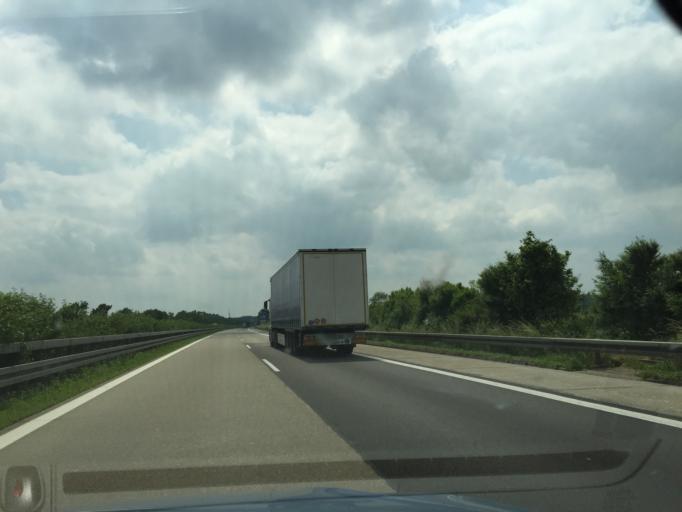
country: DE
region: Baden-Wuerttemberg
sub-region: Regierungsbezirk Stuttgart
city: Herbrechtingen
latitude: 48.5935
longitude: 10.1876
